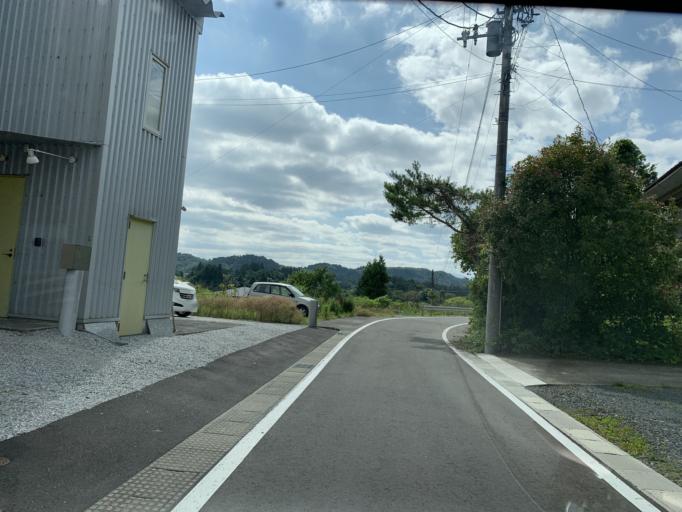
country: JP
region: Iwate
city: Ichinoseki
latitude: 38.9289
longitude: 141.0959
